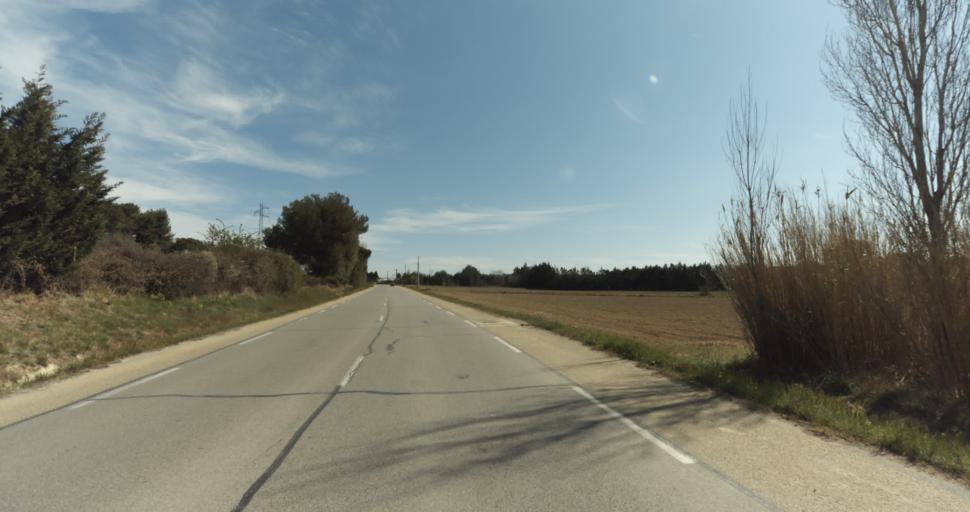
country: FR
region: Provence-Alpes-Cote d'Azur
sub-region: Departement des Bouches-du-Rhone
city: Lambesc
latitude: 43.6501
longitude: 5.2285
